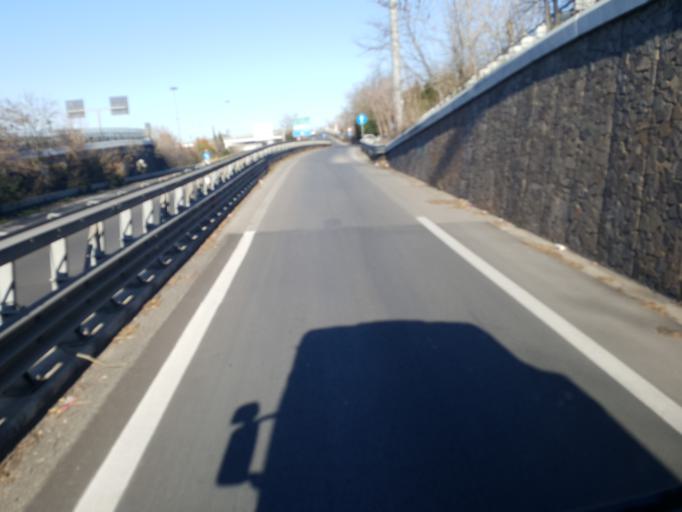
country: IT
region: Latium
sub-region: Citta metropolitana di Roma Capitale
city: Vitinia
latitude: 41.8001
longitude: 12.4176
